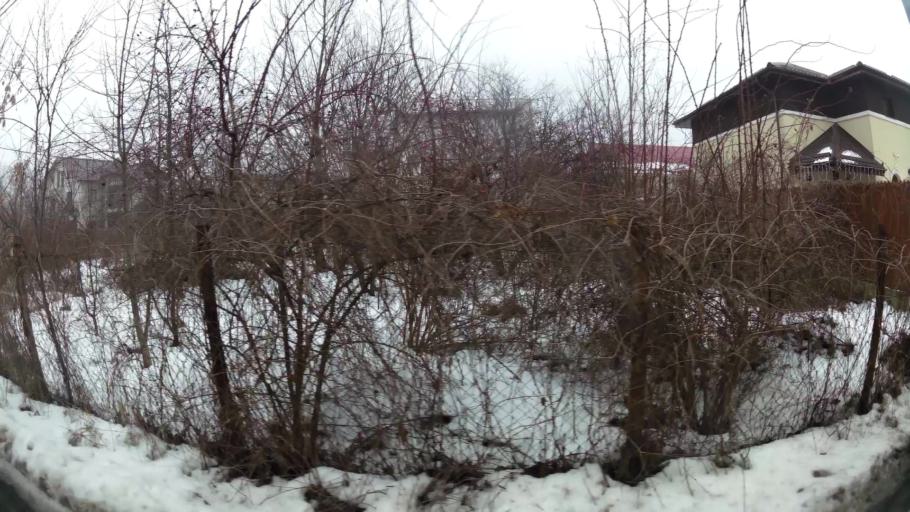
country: RO
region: Ilfov
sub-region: Comuna Chiajna
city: Rosu
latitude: 44.4381
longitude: 25.9957
